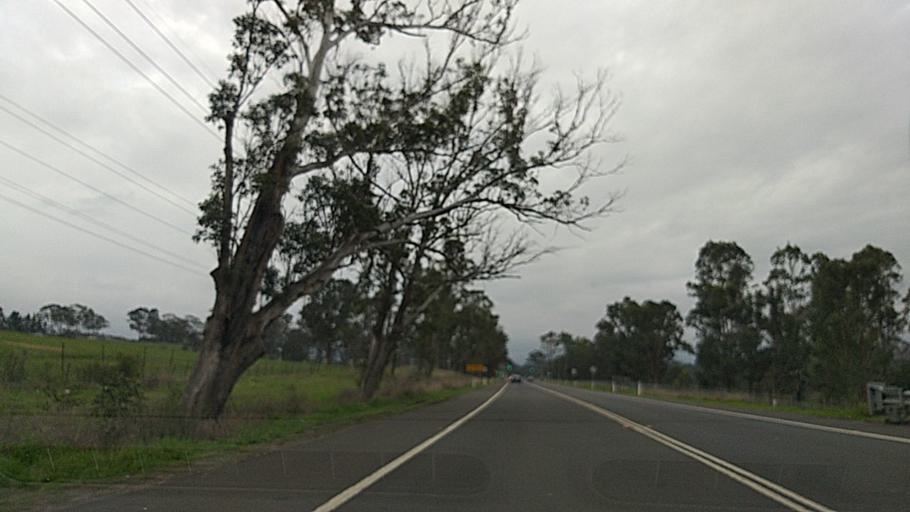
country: AU
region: New South Wales
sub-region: Penrith Municipality
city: Glenmore Park
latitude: -33.8086
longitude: 150.6950
